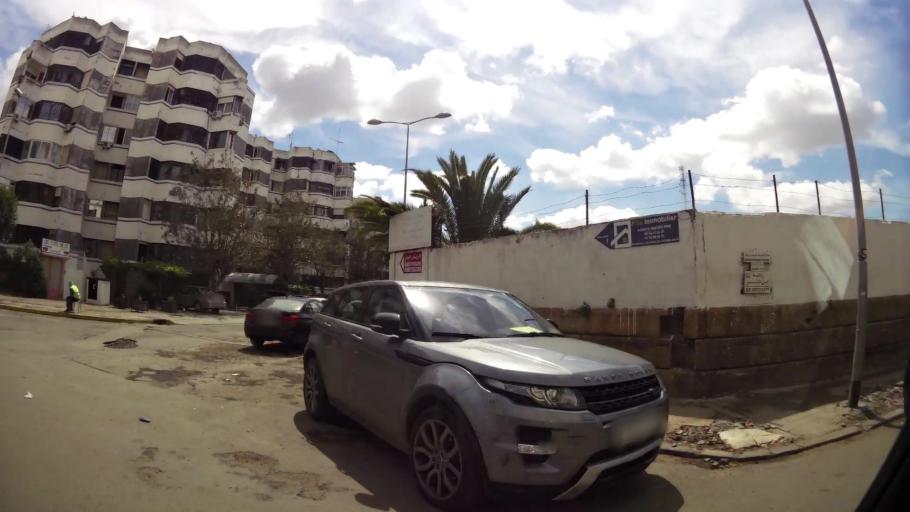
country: MA
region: Grand Casablanca
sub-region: Casablanca
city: Casablanca
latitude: 33.5745
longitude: -7.6483
